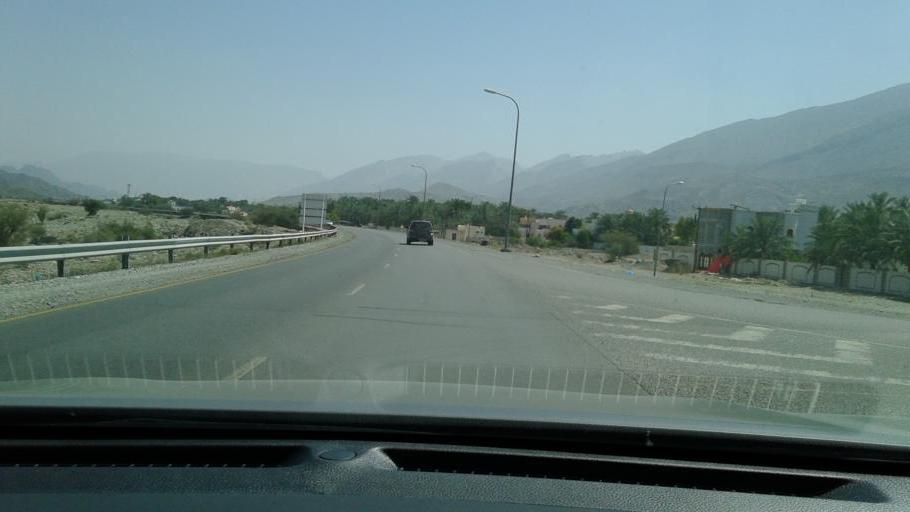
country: OM
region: Al Batinah
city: Rustaq
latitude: 23.4035
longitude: 57.4277
